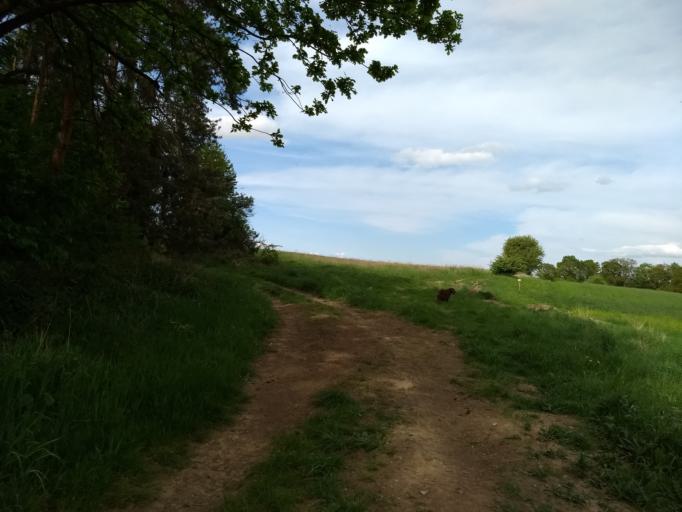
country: CZ
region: Central Bohemia
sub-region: Okres Beroun
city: Lodenice
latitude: 50.0455
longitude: 14.1623
